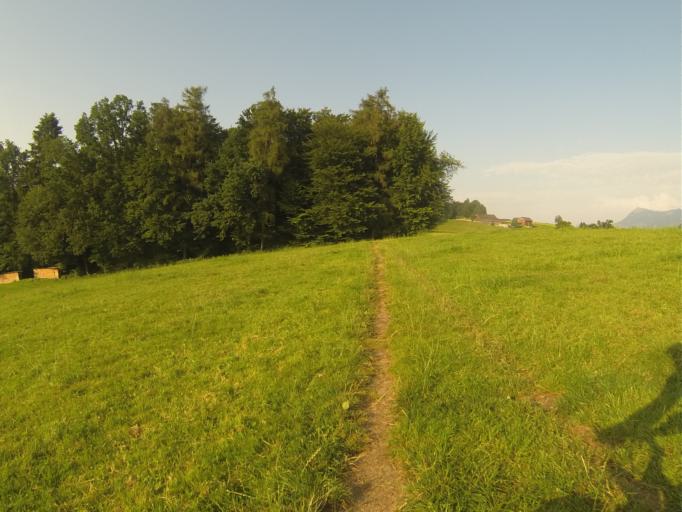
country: CH
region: Lucerne
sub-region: Lucerne-Land District
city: Ebikon
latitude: 47.0769
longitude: 8.3146
